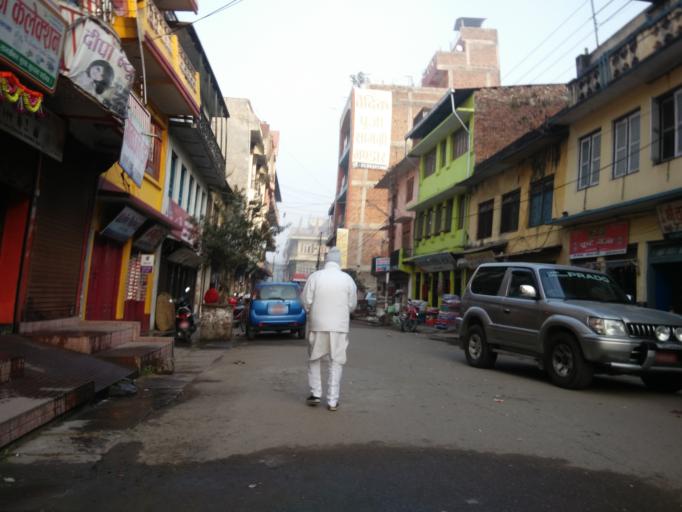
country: NP
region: Central Region
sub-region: Narayani Zone
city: Bharatpur
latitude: 27.6981
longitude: 84.4242
